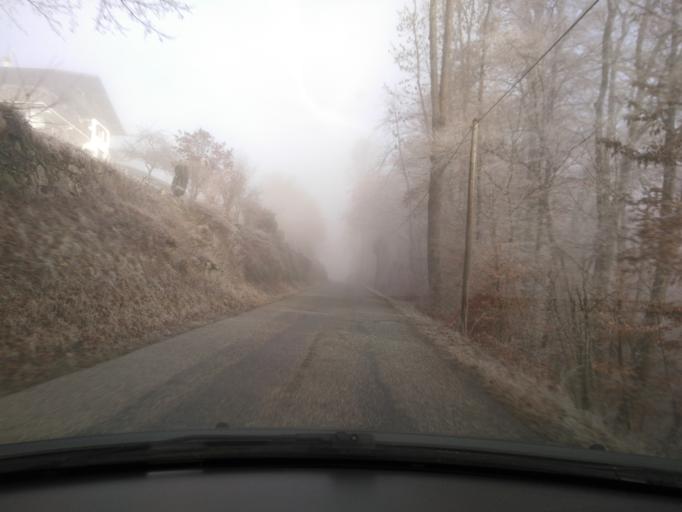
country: FR
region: Rhone-Alpes
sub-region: Departement de la Haute-Savoie
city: Sallanches
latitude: 45.9445
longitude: 6.6200
